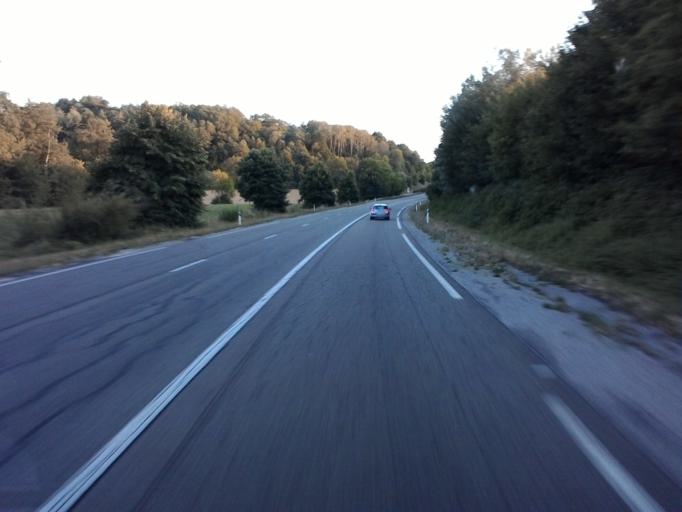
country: FR
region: Franche-Comte
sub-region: Departement du Doubs
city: Quingey
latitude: 47.0929
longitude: 5.8924
